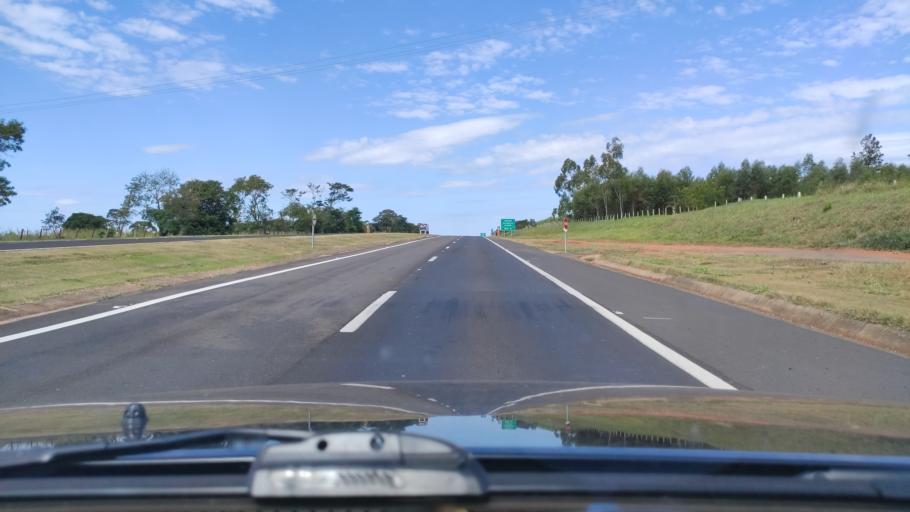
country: BR
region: Sao Paulo
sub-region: Rancharia
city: Rancharia
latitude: -22.4785
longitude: -50.9343
